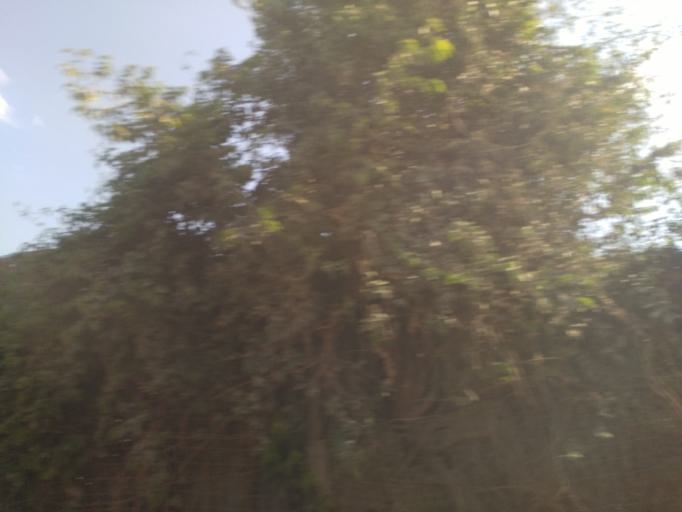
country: TZ
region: Pwani
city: Vikindu
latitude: -6.9191
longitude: 39.2650
